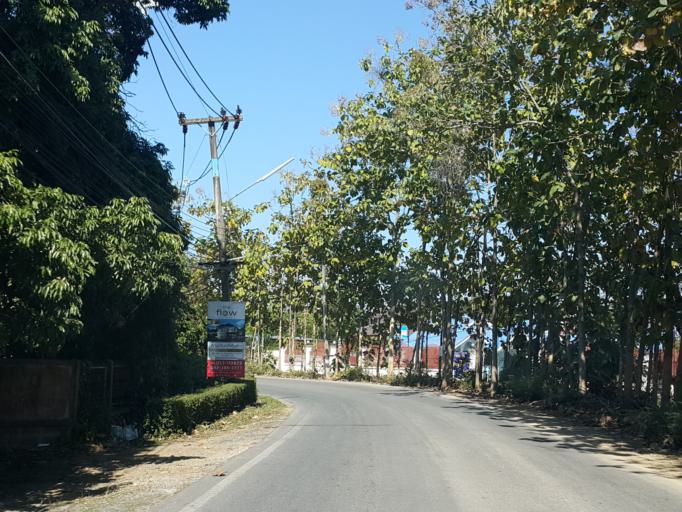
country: TH
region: Chiang Mai
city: San Sai
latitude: 18.8488
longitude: 98.9877
